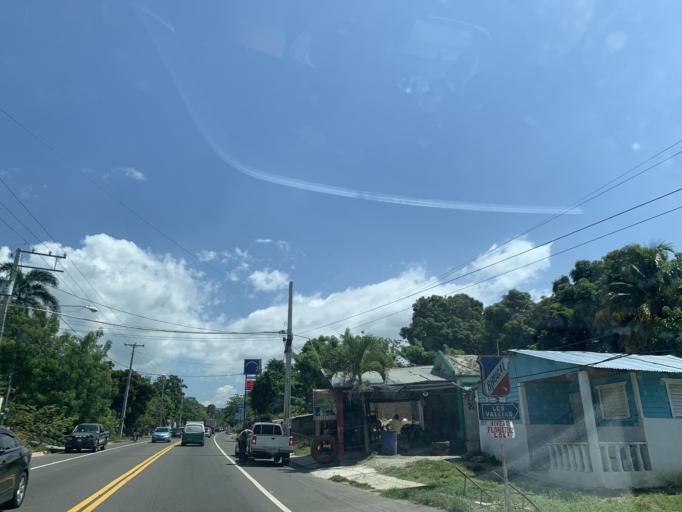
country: DO
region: Puerto Plata
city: Imbert
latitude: 19.7178
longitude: -70.8339
